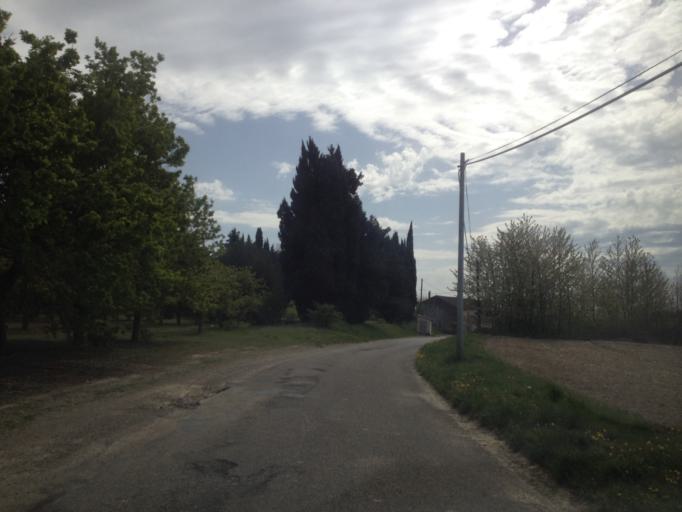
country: FR
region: Provence-Alpes-Cote d'Azur
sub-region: Departement du Vaucluse
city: Caderousse
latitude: 44.1190
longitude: 4.7816
